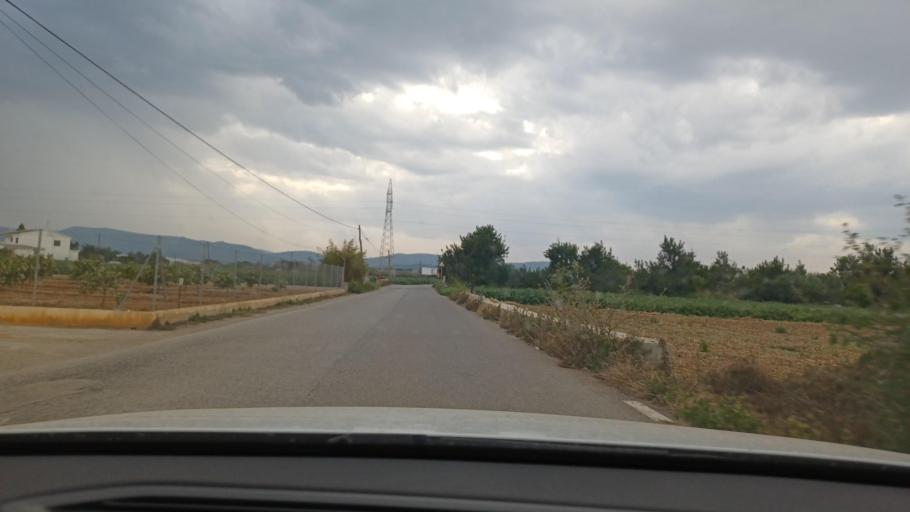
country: ES
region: Valencia
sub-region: Provincia de Castello
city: Benicarlo
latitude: 40.4075
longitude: 0.3980
